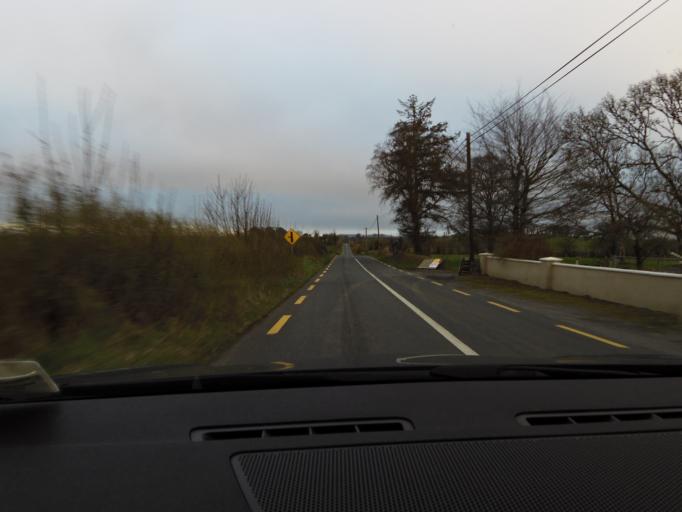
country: IE
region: Connaught
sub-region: Sligo
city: Ballymote
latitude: 54.0151
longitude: -8.5555
